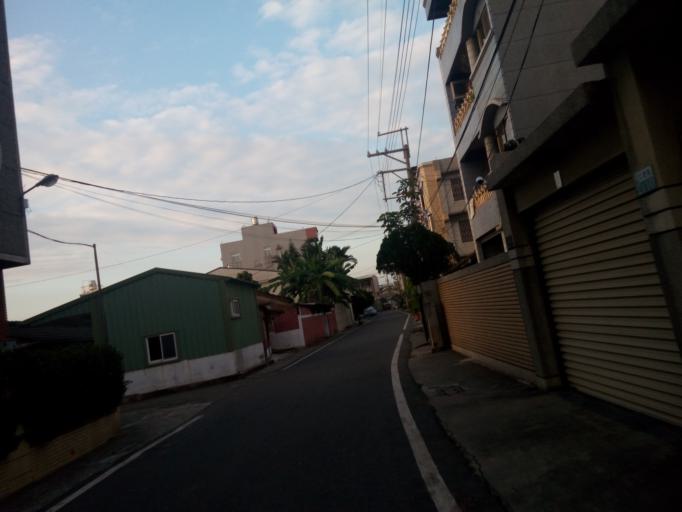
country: TW
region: Taiwan
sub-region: Chiayi
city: Jiayi Shi
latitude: 23.4977
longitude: 120.3872
